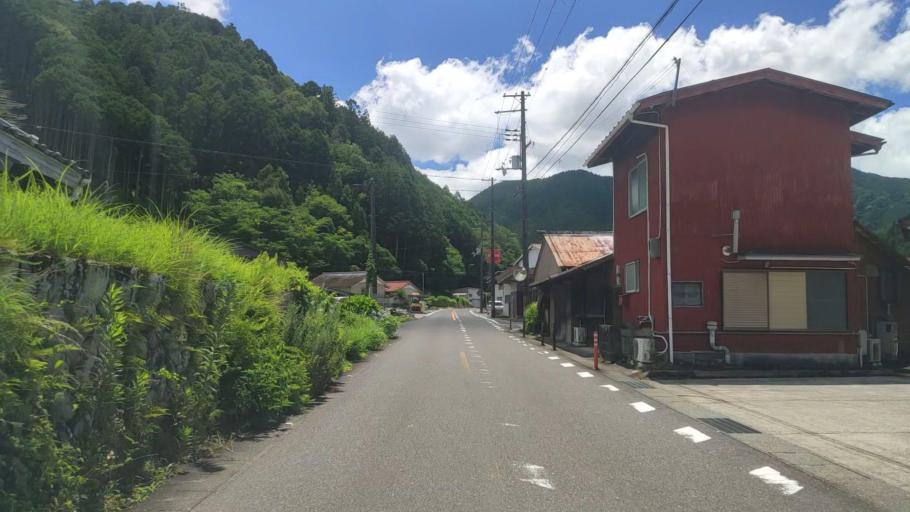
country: JP
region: Mie
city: Owase
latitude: 33.9841
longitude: 136.0487
